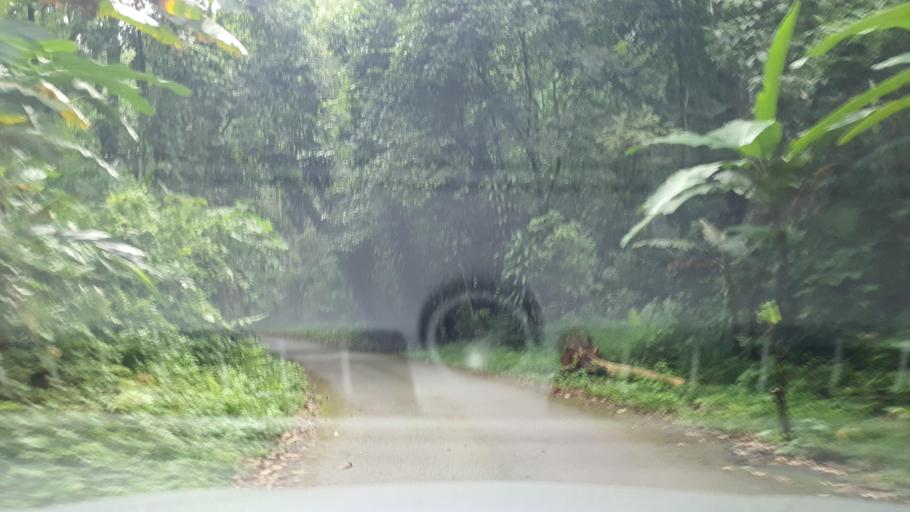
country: TH
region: Chiang Mai
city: Mae On
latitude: 18.9447
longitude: 99.3088
